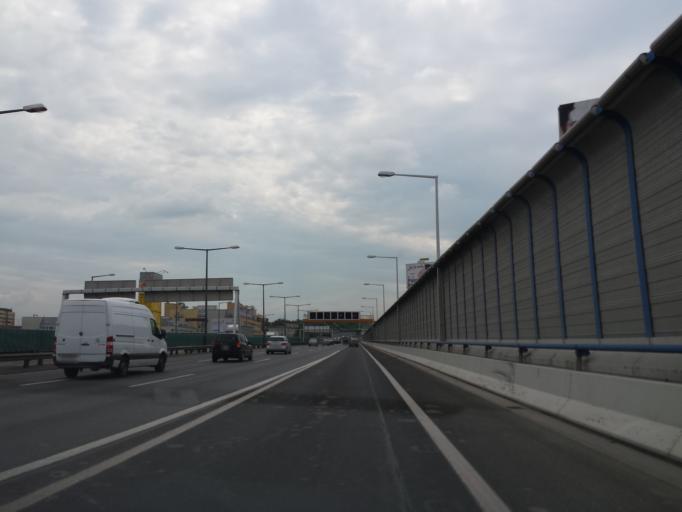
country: AT
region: Vienna
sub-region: Wien Stadt
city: Vienna
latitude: 48.1781
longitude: 16.3999
